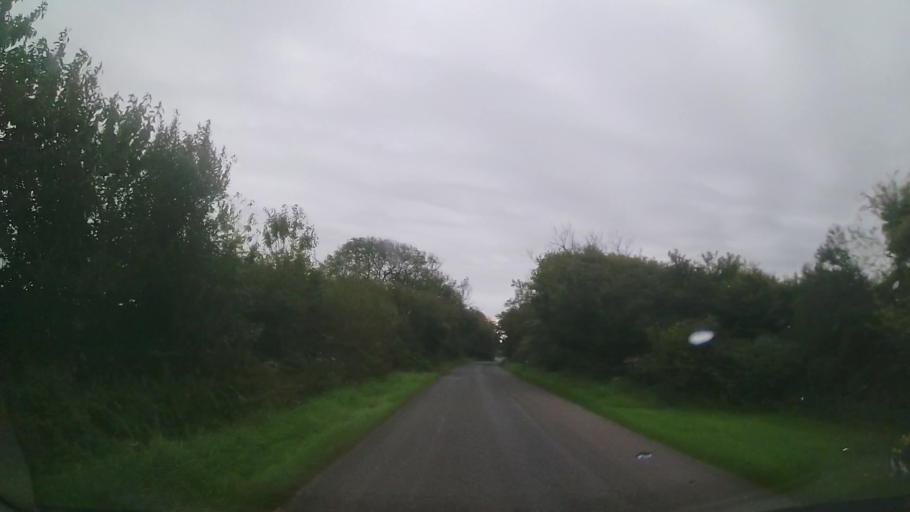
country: GB
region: Wales
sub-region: Carmarthenshire
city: Whitland
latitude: 51.7509
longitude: -4.6017
